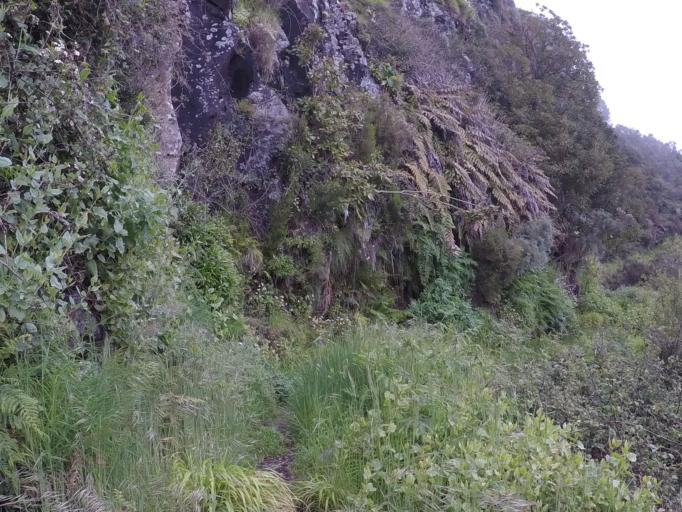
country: PT
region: Madeira
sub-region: Camara de Lobos
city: Curral das Freiras
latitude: 32.7338
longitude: -16.9906
